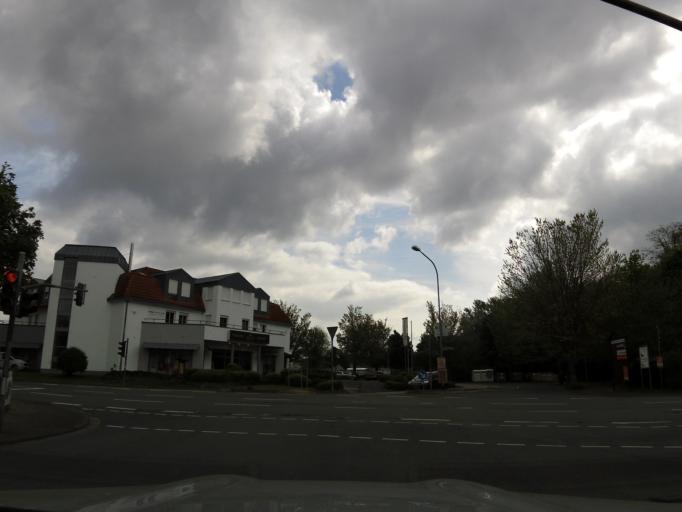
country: DE
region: Hesse
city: Burgsolms
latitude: 50.5427
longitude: 8.4086
